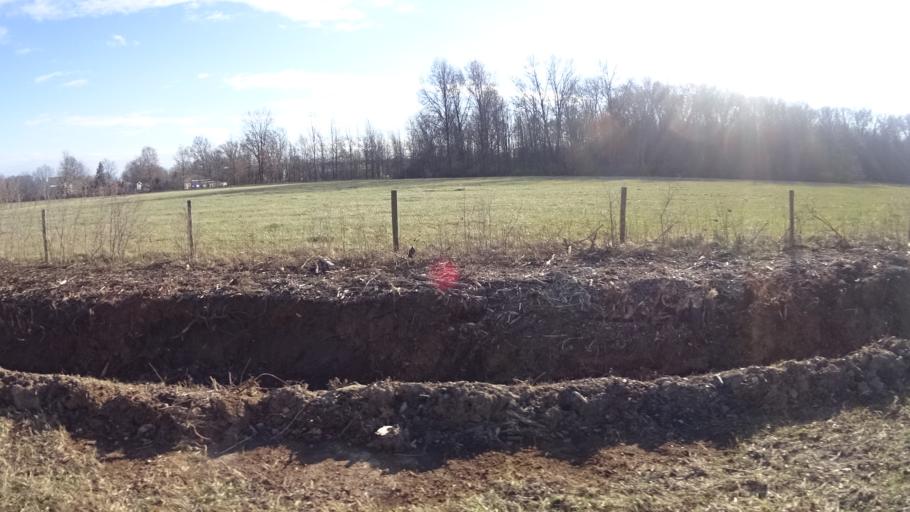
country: US
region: Ohio
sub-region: Lorain County
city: North Ridgeville
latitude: 41.4082
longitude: -82.0517
